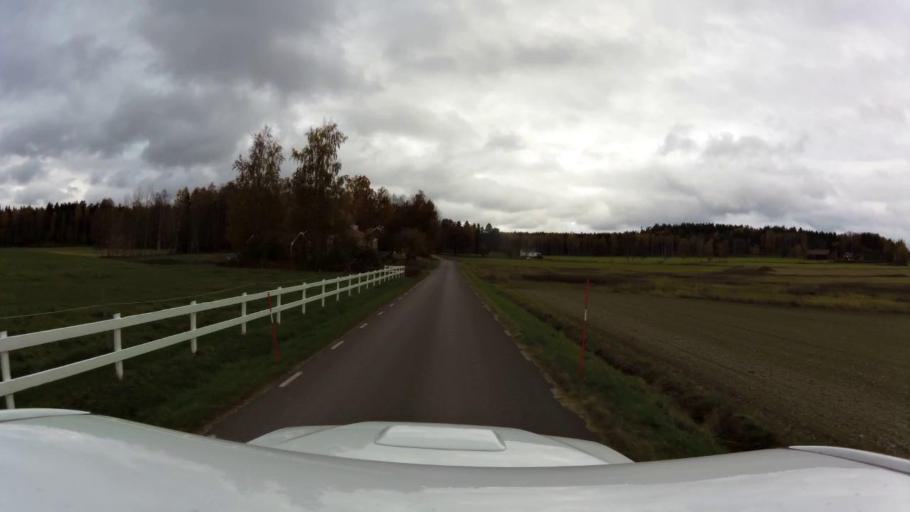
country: SE
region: OEstergoetland
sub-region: Motala Kommun
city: Borensberg
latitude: 58.5727
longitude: 15.3901
